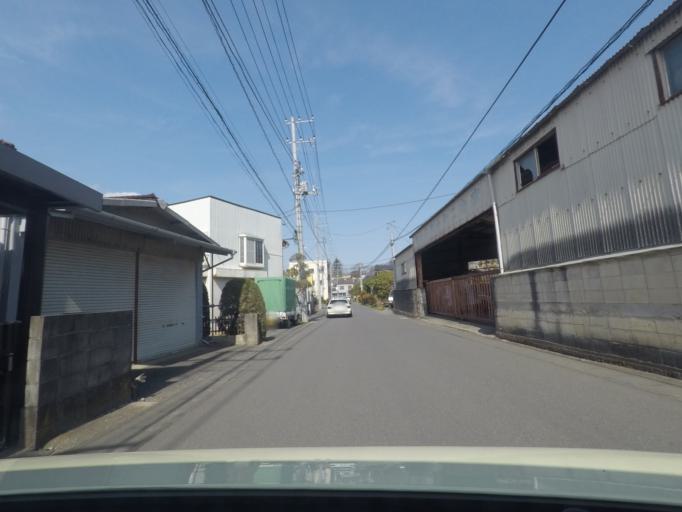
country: JP
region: Ibaraki
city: Ishioka
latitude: 36.1684
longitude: 140.3579
